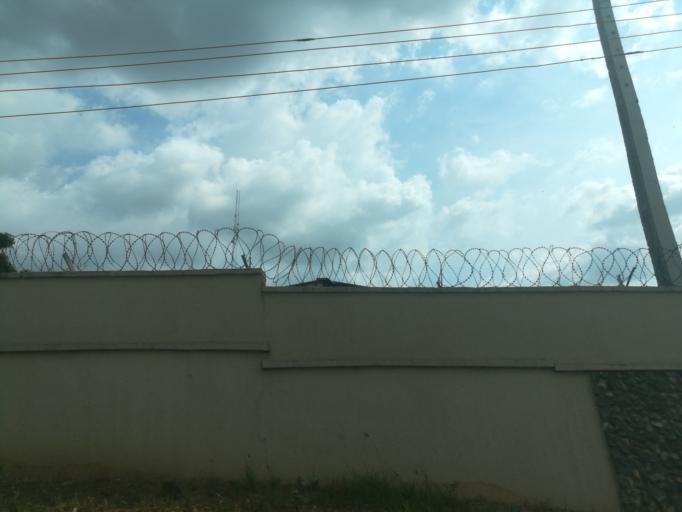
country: NG
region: Oyo
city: Ibadan
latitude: 7.3643
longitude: 3.8534
